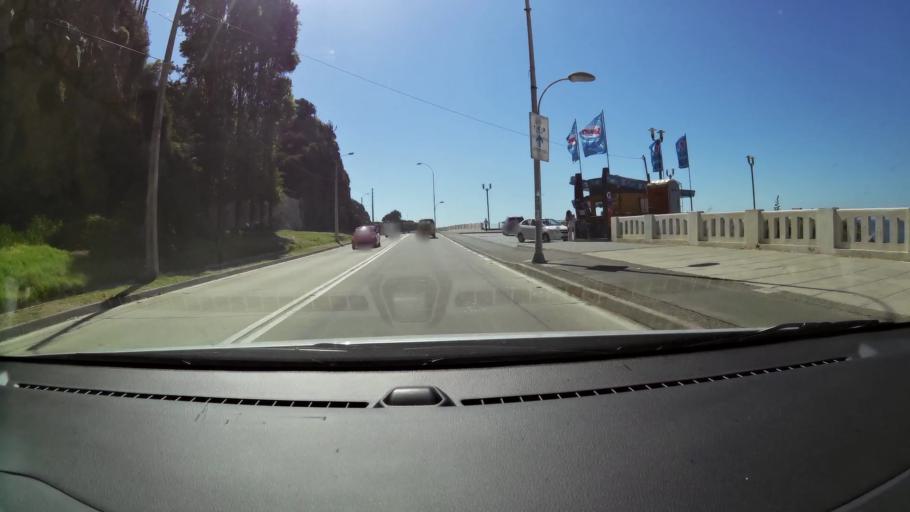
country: CL
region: Valparaiso
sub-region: Provincia de Valparaiso
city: Valparaiso
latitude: -33.0202
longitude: -71.6344
